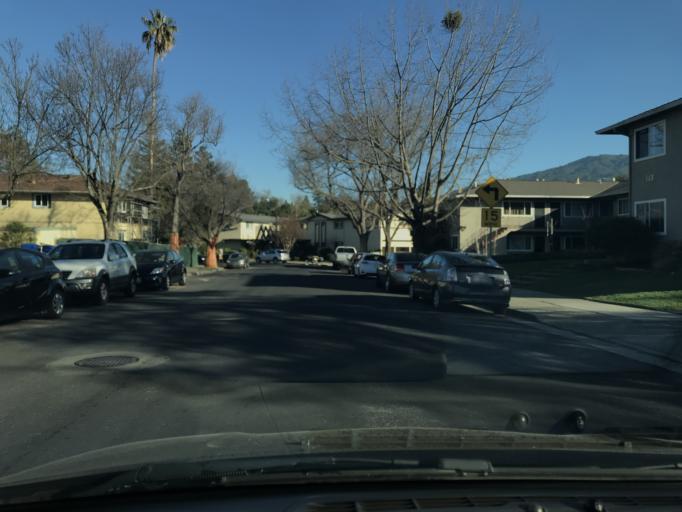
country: US
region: California
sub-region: Santa Clara County
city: Los Gatos
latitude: 37.2303
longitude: -121.9754
